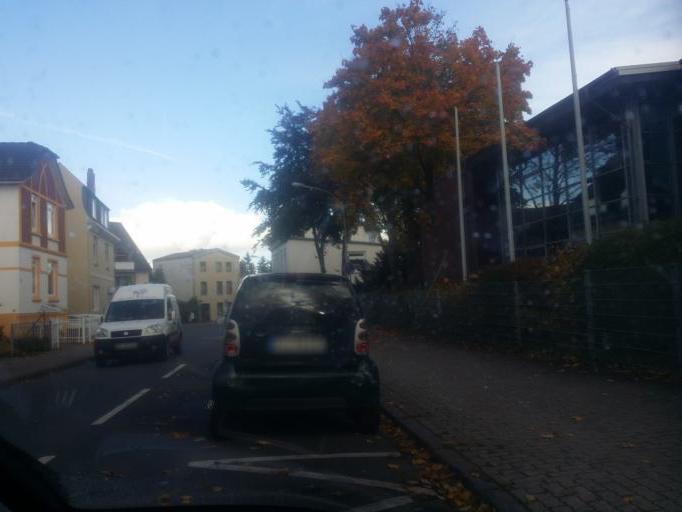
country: DE
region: Schleswig-Holstein
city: Pinneberg
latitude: 53.6579
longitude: 9.7852
